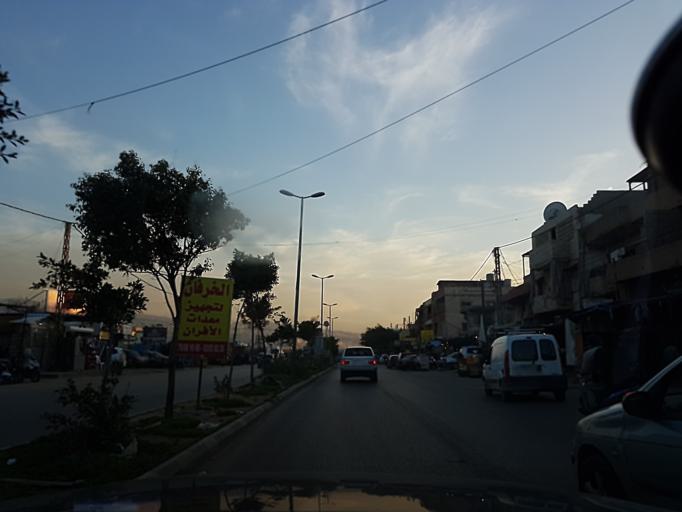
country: LB
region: Beyrouth
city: Beirut
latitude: 33.8303
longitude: 35.4843
